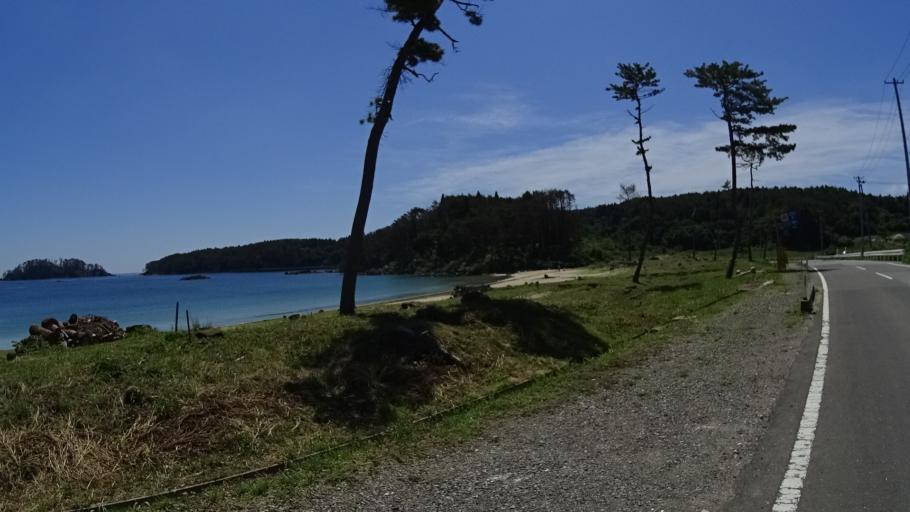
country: JP
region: Iwate
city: Ofunato
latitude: 38.8520
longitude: 141.6217
